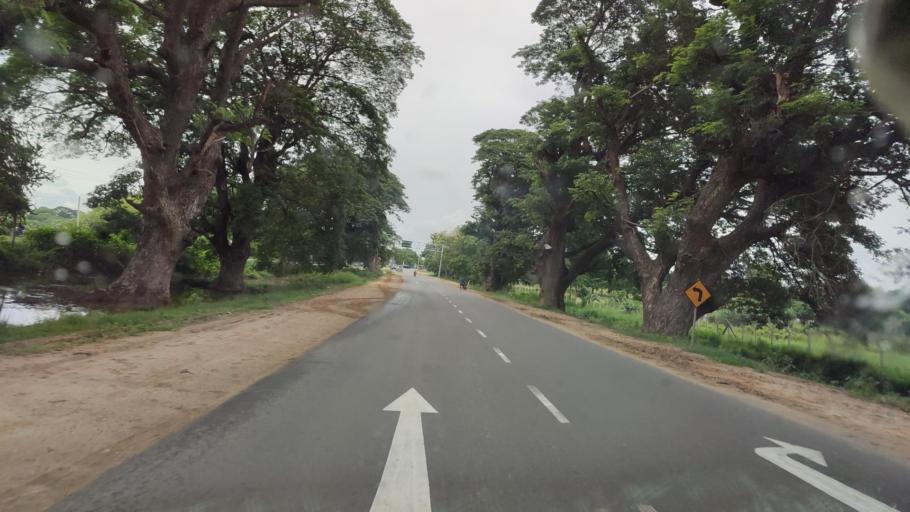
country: MM
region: Mandalay
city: Meiktila
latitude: 20.7928
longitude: 95.9109
